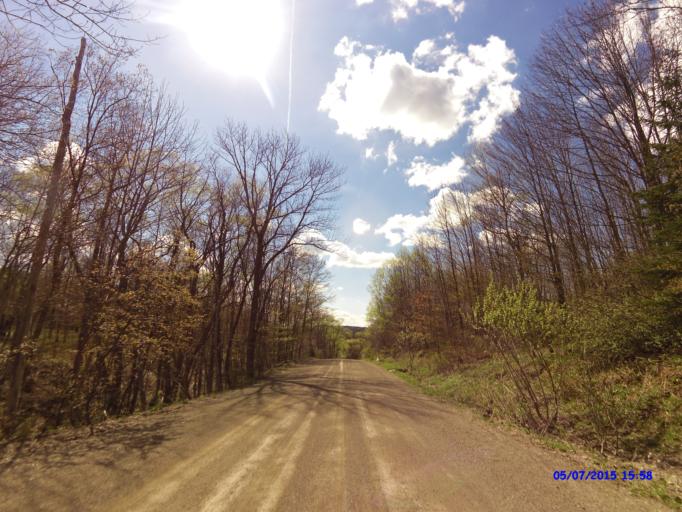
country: US
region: New York
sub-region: Cattaraugus County
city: Franklinville
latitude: 42.2976
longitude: -78.5780
